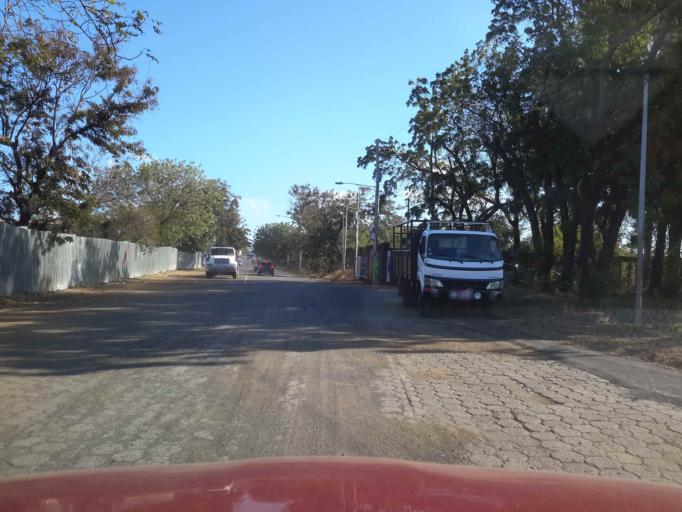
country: NI
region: Managua
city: Managua
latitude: 12.1334
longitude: -86.2719
